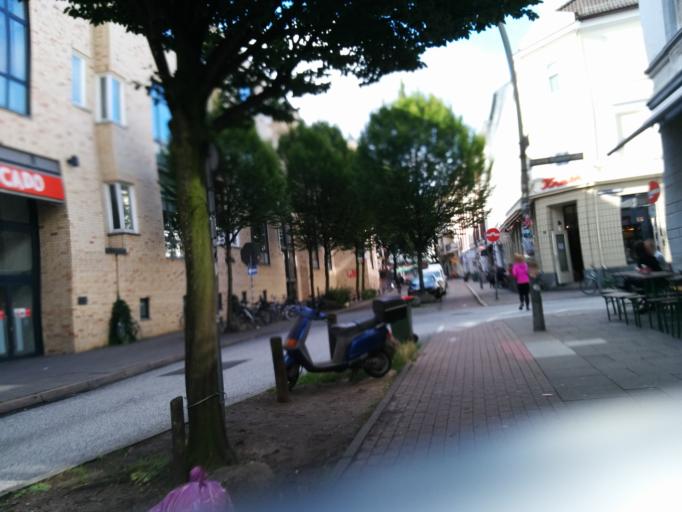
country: DE
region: Hamburg
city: Altona
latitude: 53.5533
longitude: 9.9314
